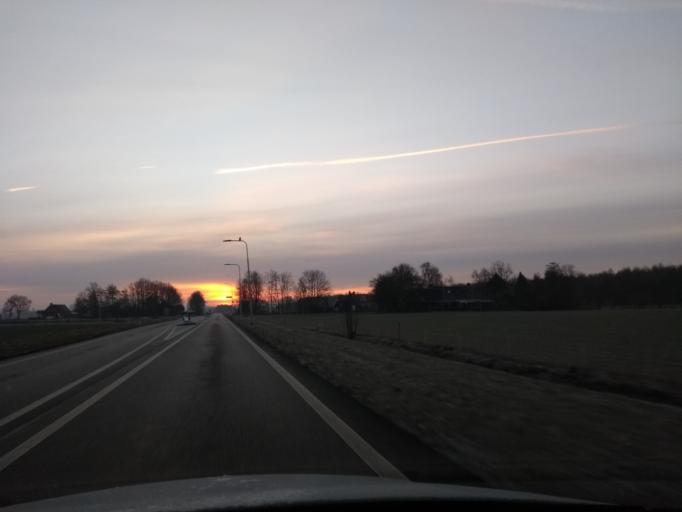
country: NL
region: Friesland
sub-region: Gemeente Gaasterlan-Sleat
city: Balk
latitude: 52.8842
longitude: 5.5973
